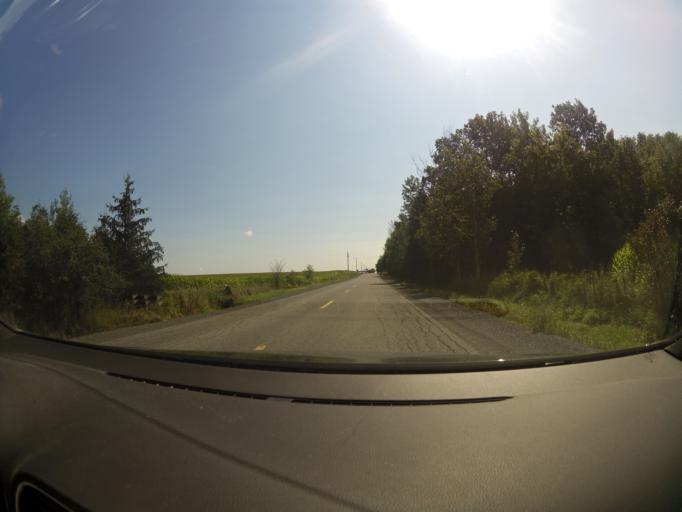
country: CA
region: Ontario
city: Arnprior
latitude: 45.3713
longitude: -76.2580
